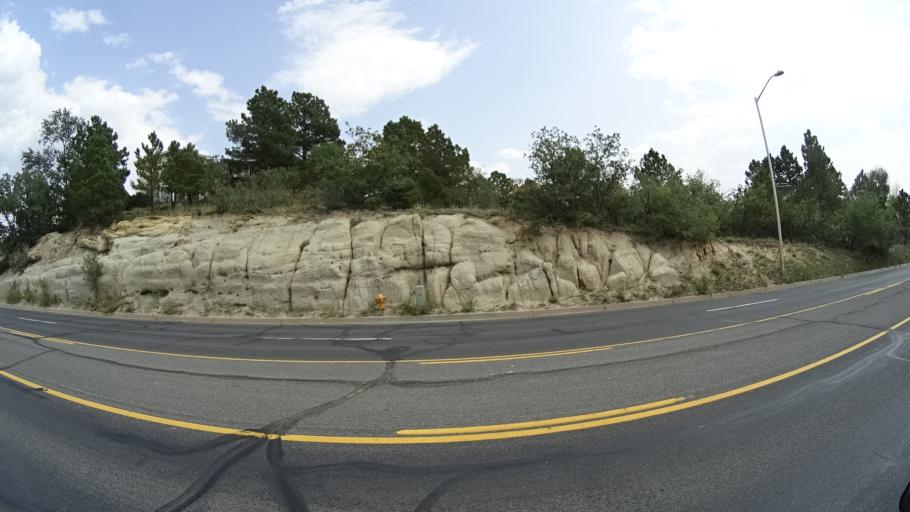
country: US
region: Colorado
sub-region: El Paso County
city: Cimarron Hills
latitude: 38.8645
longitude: -104.7480
